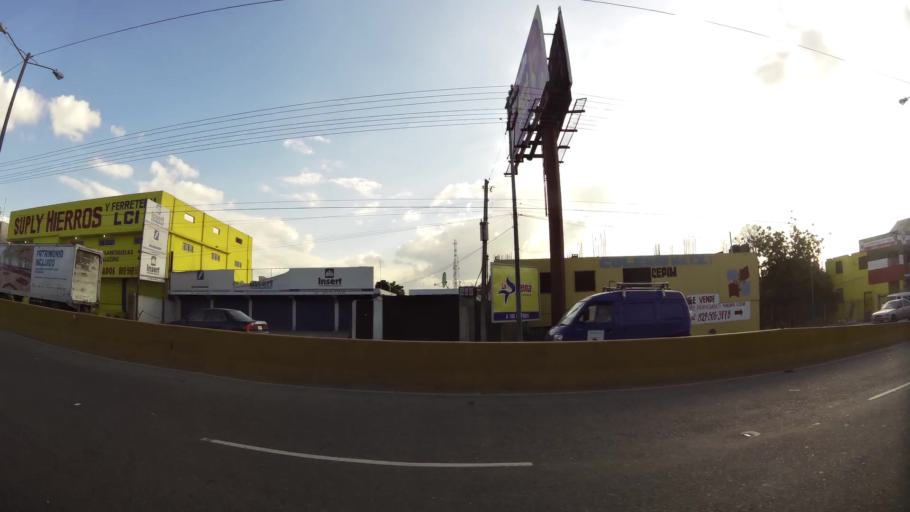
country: DO
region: Nacional
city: Ensanche Luperon
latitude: 18.5461
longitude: -69.9027
